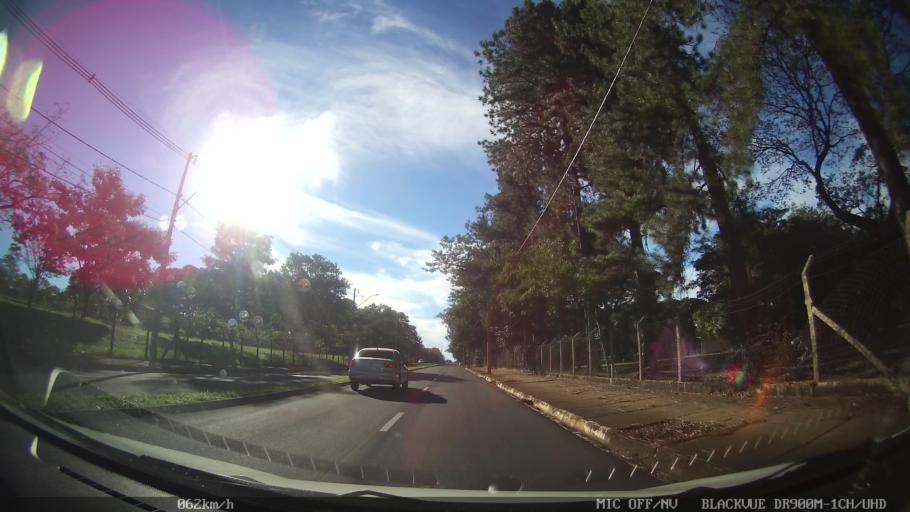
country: BR
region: Sao Paulo
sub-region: Araraquara
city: Araraquara
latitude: -21.7545
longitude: -48.1816
